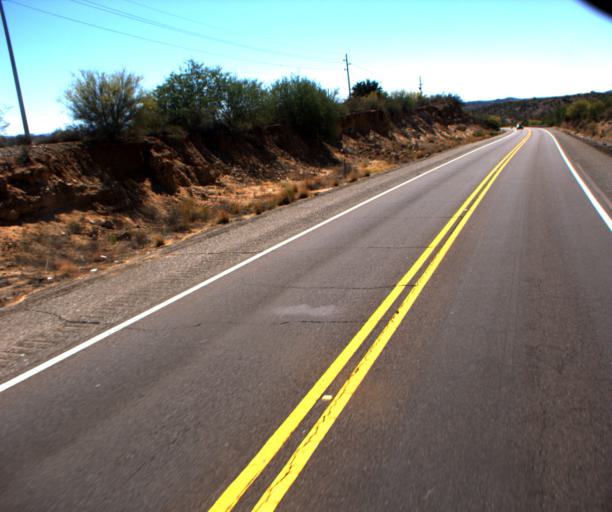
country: US
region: Arizona
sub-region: Maricopa County
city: Wickenburg
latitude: 33.9958
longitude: -112.7556
